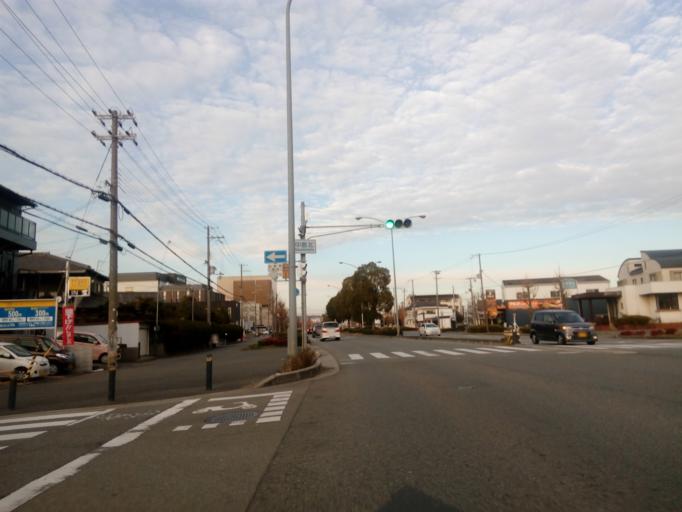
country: JP
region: Hyogo
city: Himeji
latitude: 34.7972
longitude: 134.6774
